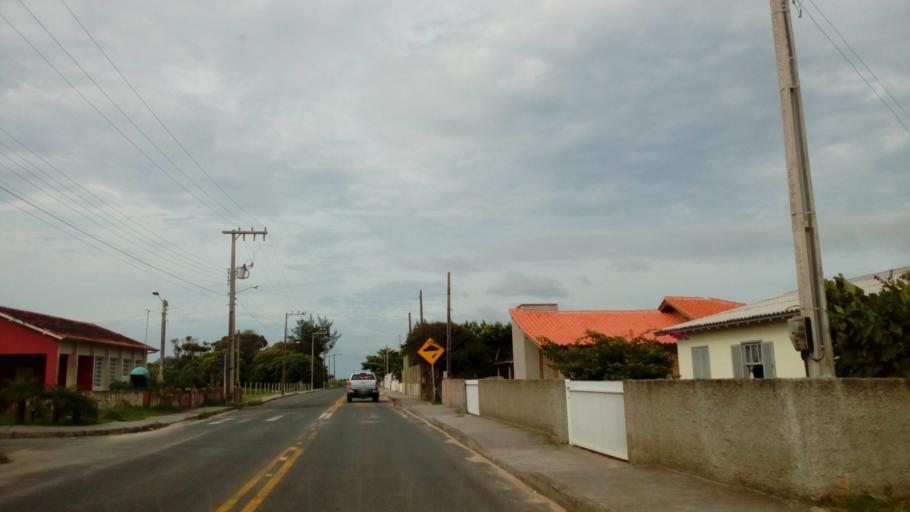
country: BR
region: Santa Catarina
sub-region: Laguna
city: Laguna
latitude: -28.5760
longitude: -48.8213
